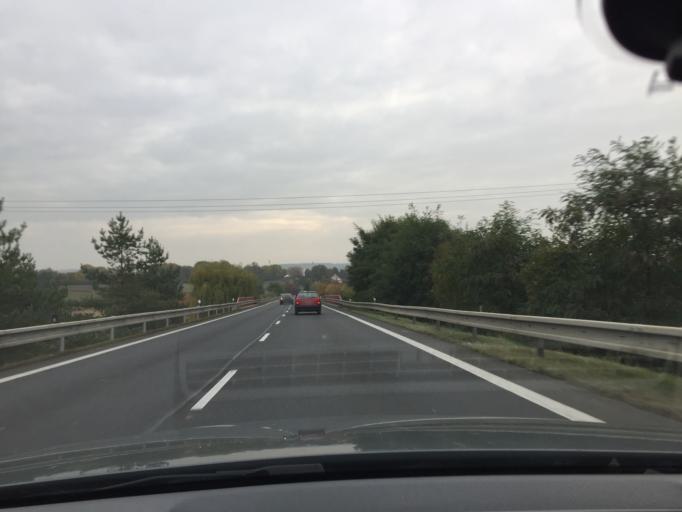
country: CZ
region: Ustecky
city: Rehlovice
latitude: 50.5875
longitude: 13.9112
